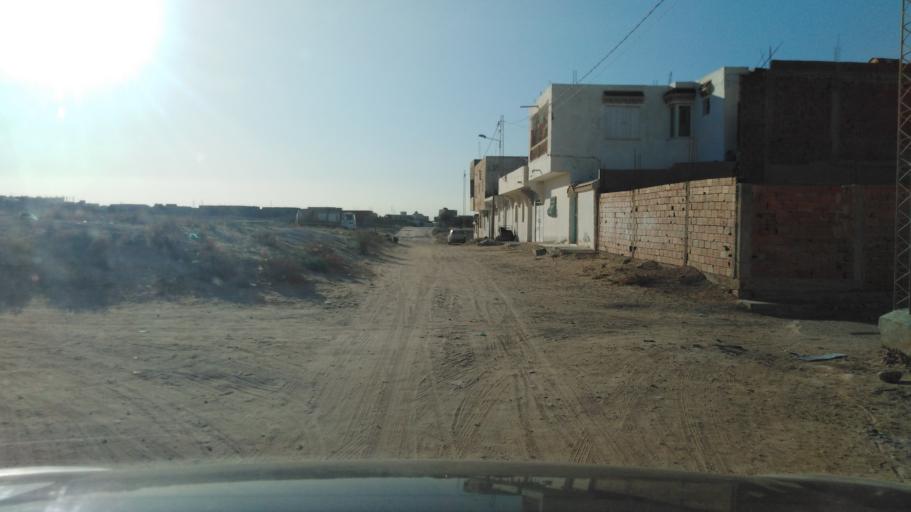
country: TN
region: Qabis
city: Gabes
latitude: 33.9531
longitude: 10.0086
